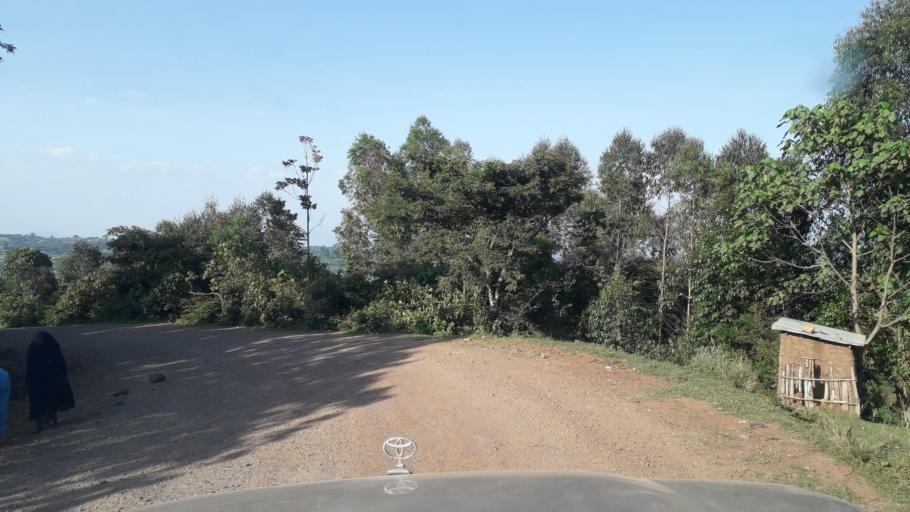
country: ET
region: Oromiya
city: Jima
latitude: 7.4665
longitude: 36.8767
